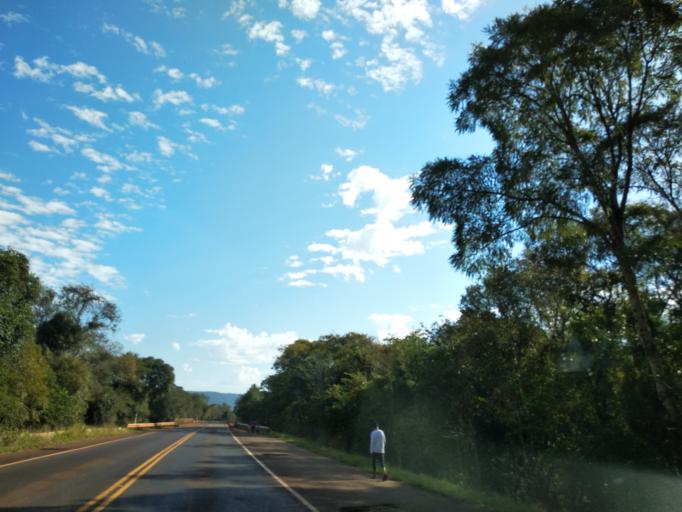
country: AR
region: Misiones
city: Aristobulo del Valle
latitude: -27.1019
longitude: -54.9630
